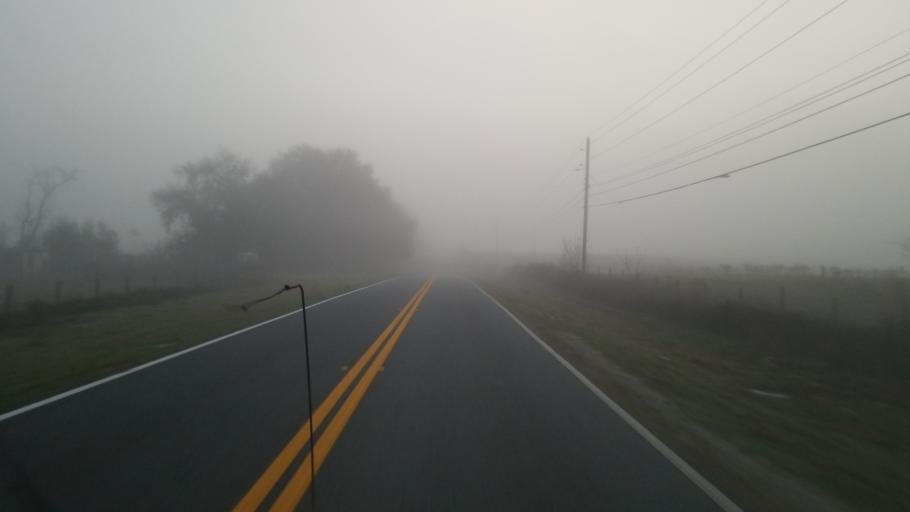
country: US
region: Florida
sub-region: Marion County
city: Ocala
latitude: 29.1502
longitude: -82.2362
